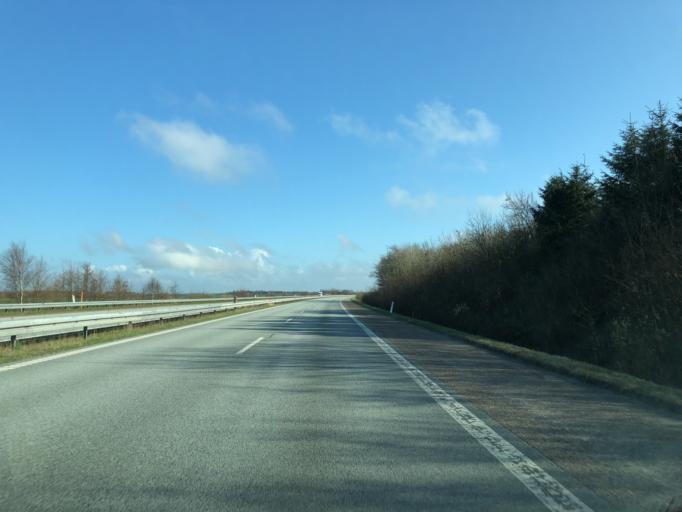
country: DK
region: North Denmark
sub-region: Hjorring Kommune
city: Hjorring
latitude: 57.4775
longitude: 10.0408
